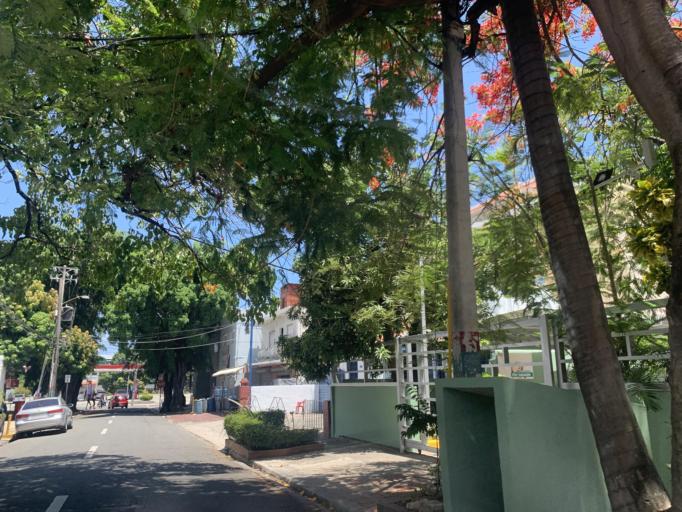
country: DO
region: Nacional
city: Ciudad Nueva
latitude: 18.4629
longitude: -69.9051
